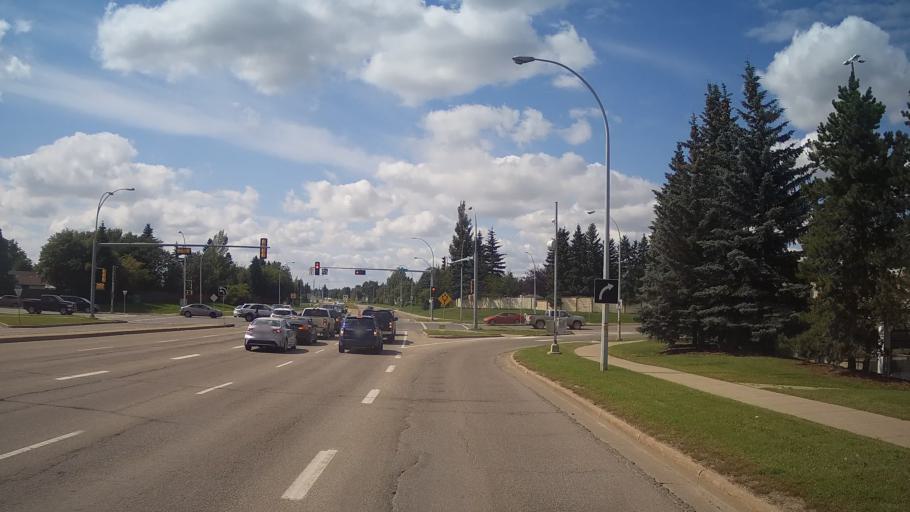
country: CA
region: Alberta
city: St. Albert
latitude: 53.5212
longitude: -113.6292
